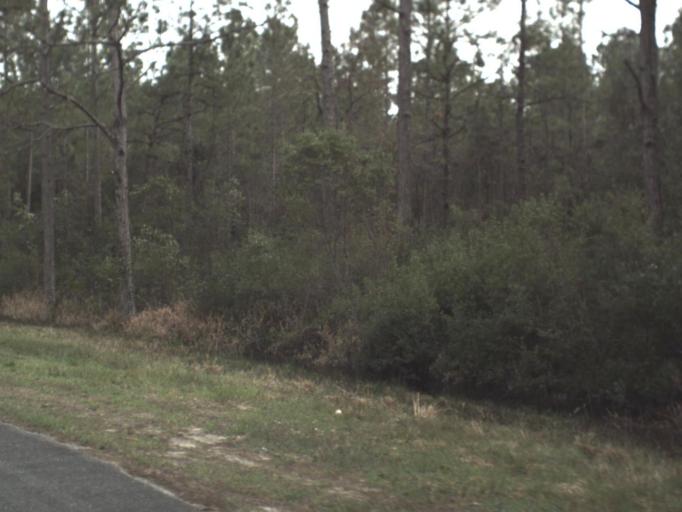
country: US
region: Florida
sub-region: Gadsden County
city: Midway
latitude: 30.3778
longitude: -84.5596
